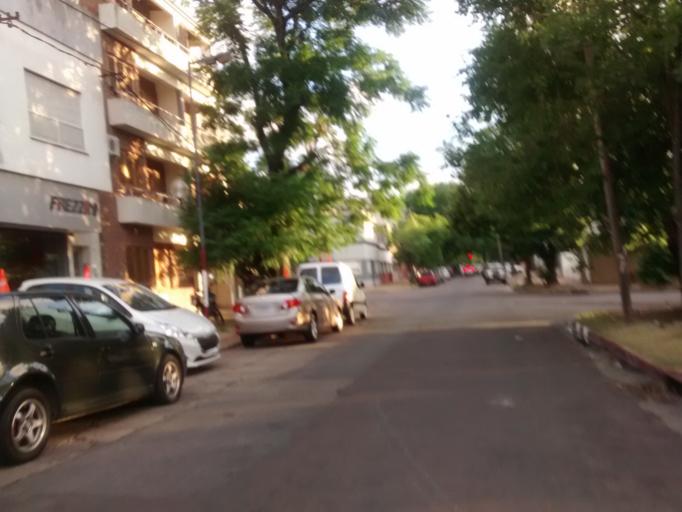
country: AR
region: Buenos Aires
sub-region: Partido de La Plata
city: La Plata
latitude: -34.9199
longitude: -57.9674
